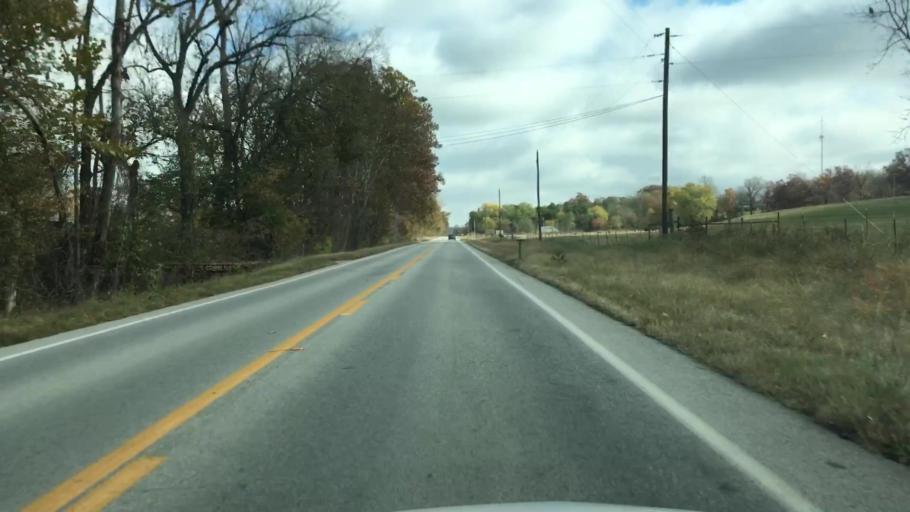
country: US
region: Arkansas
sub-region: Benton County
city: Gentry
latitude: 36.2575
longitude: -94.3999
